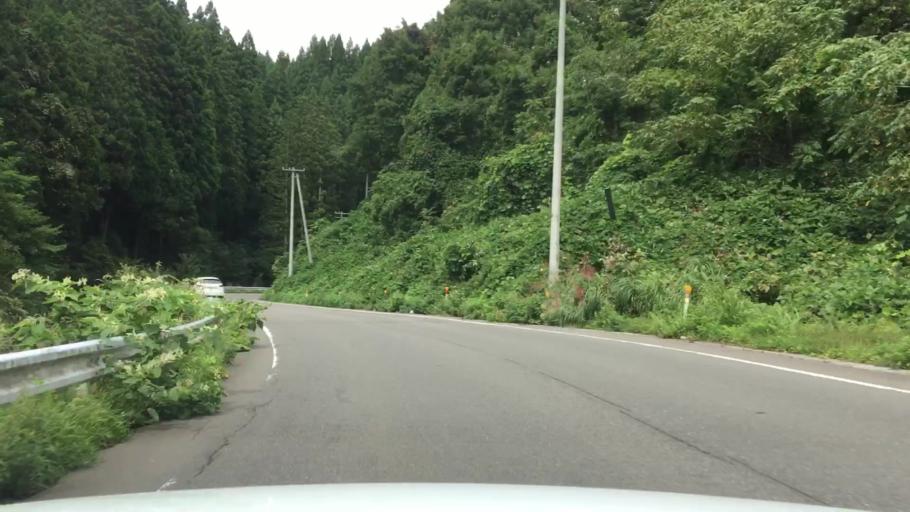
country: JP
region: Aomori
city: Shimokizukuri
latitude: 40.7333
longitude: 140.2509
